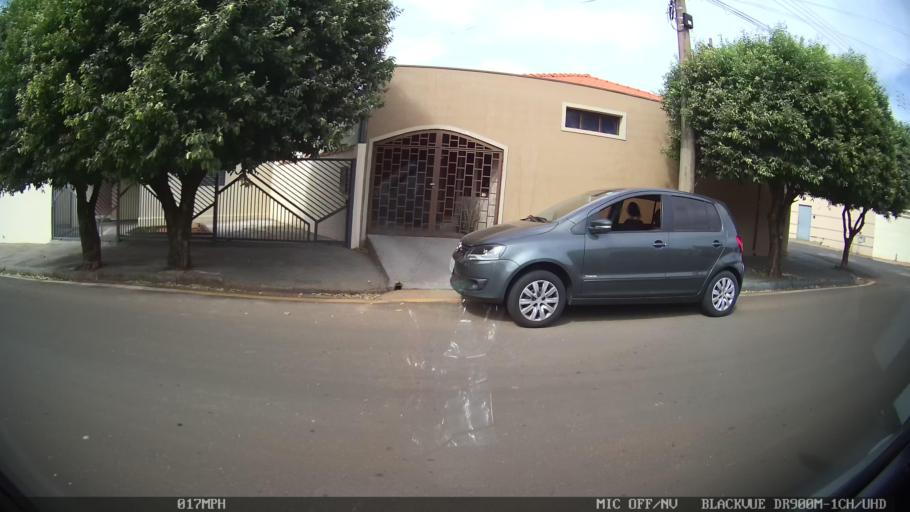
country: BR
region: Sao Paulo
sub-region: Catanduva
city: Catanduva
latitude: -21.1472
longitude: -48.9709
